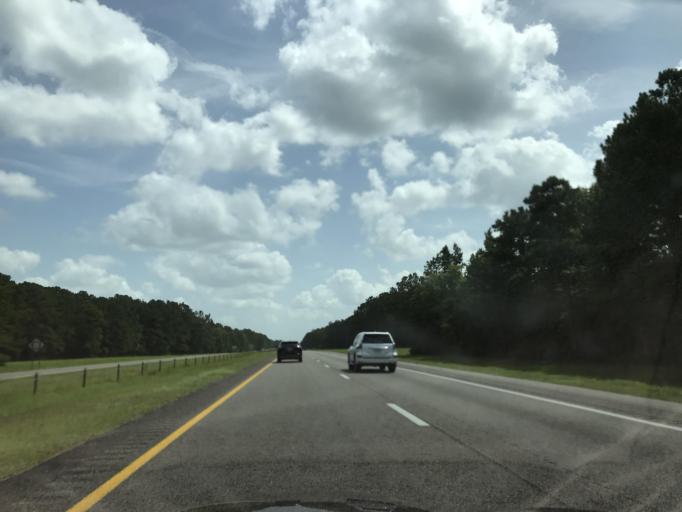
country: US
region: North Carolina
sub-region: Pender County
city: Burgaw
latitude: 34.5758
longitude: -77.9020
